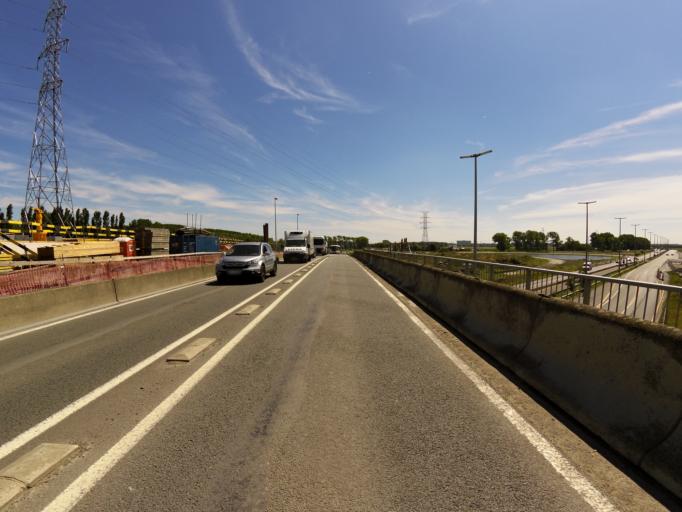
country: BE
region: Flanders
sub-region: Provincie West-Vlaanderen
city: Zuienkerke
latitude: 51.2556
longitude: 3.1906
